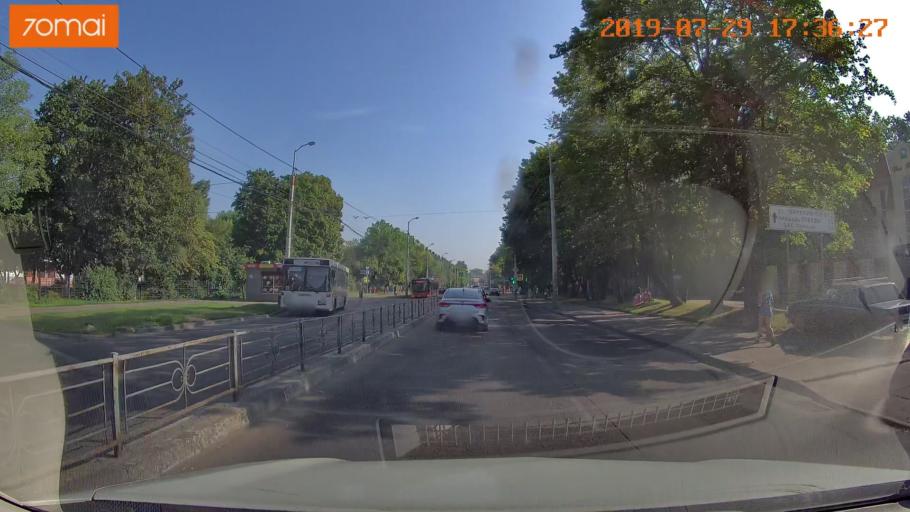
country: RU
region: Kaliningrad
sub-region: Gorod Kaliningrad
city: Kaliningrad
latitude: 54.7299
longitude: 20.5102
